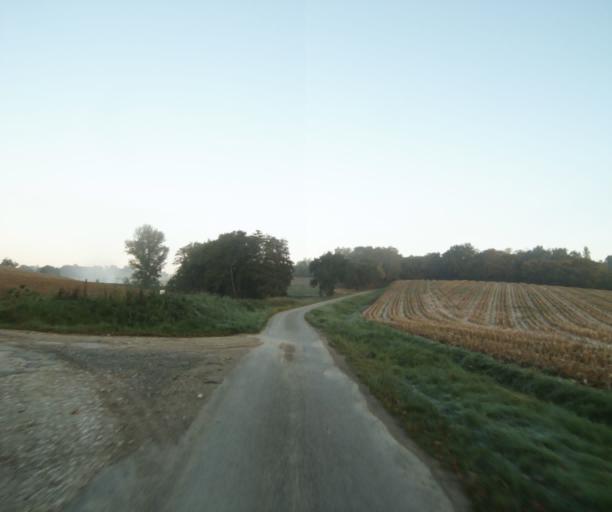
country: FR
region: Midi-Pyrenees
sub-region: Departement du Gers
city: Vic-Fezensac
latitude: 43.7925
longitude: 0.2339
